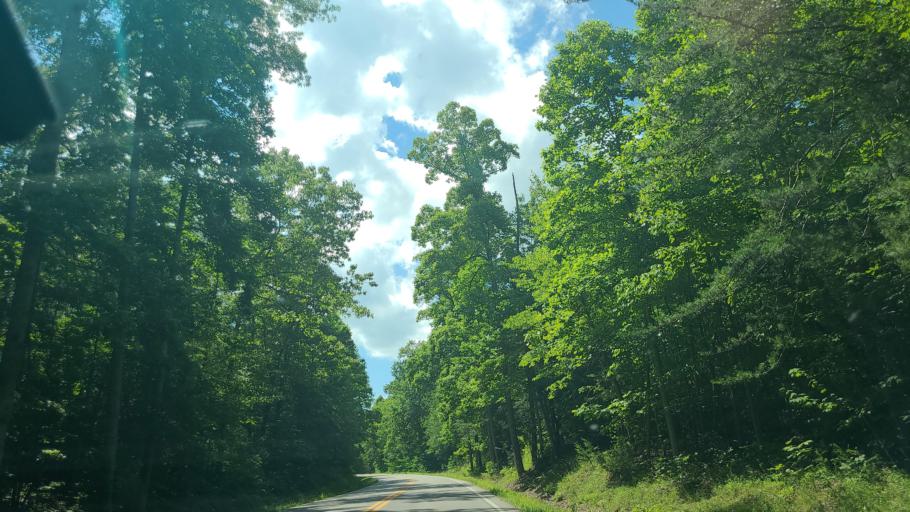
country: US
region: Kentucky
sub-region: Whitley County
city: Williamsburg
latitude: 36.8390
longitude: -84.2735
